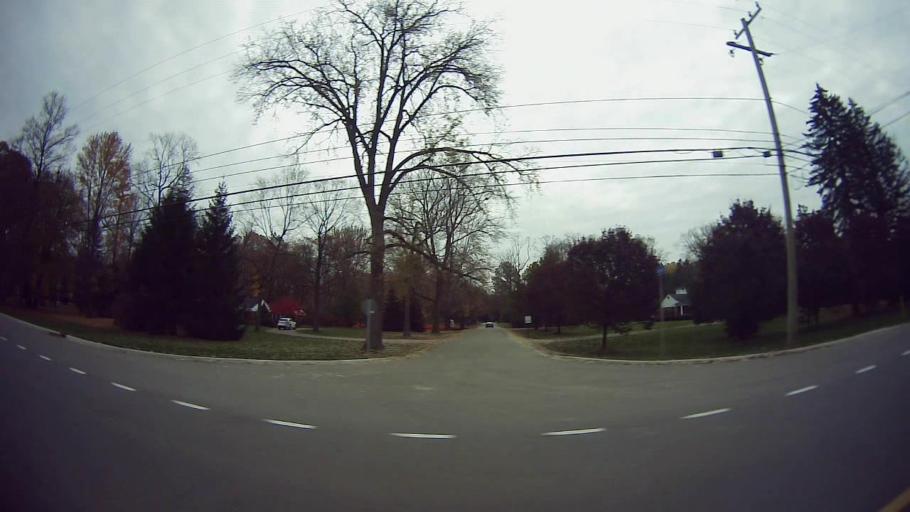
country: US
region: Michigan
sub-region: Oakland County
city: Bingham Farms
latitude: 42.5223
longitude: -83.2634
